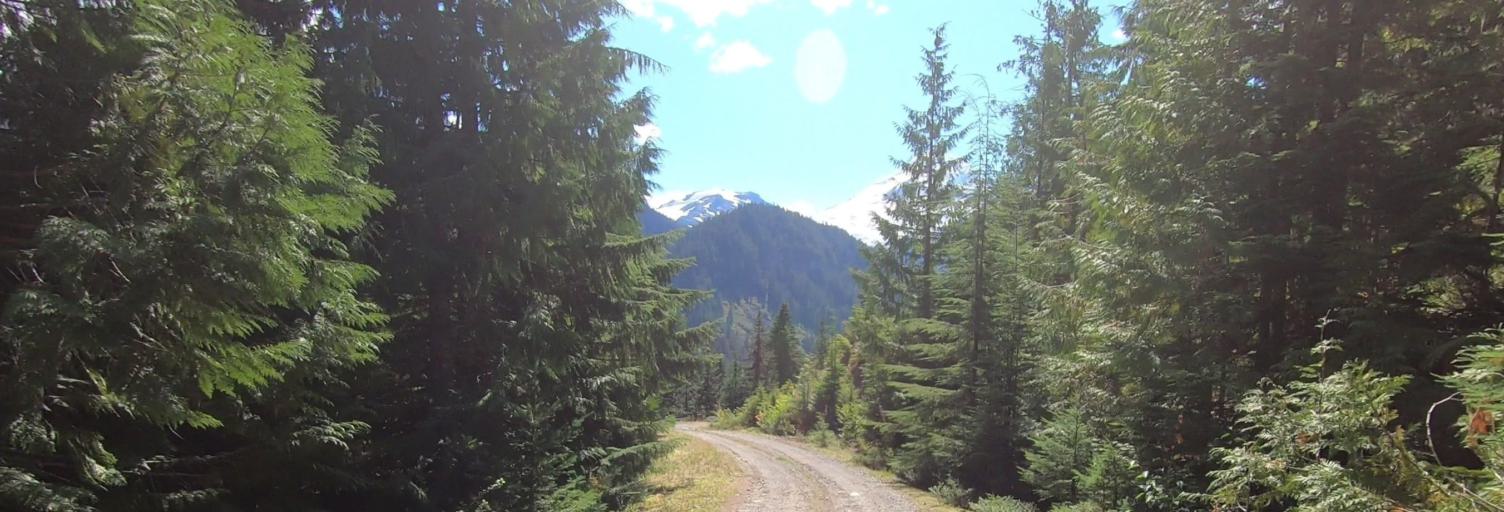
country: CA
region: British Columbia
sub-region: Fraser Valley Regional District
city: Chilliwack
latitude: 48.8665
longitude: -121.7735
